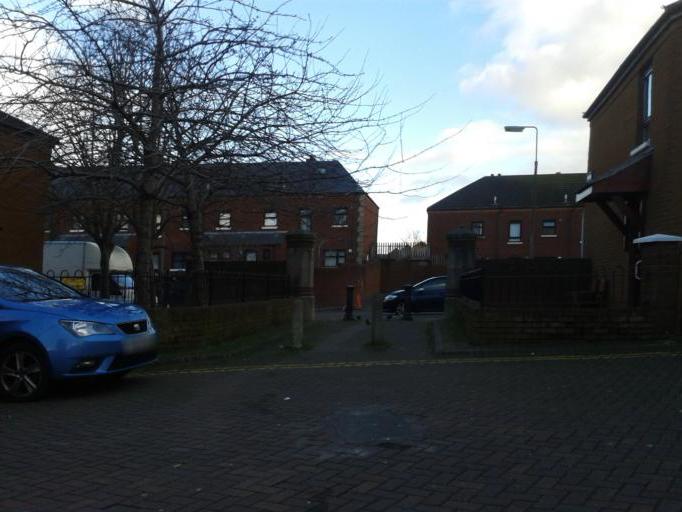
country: GB
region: Northern Ireland
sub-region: City of Belfast
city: Belfast
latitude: 54.5947
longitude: -5.9253
